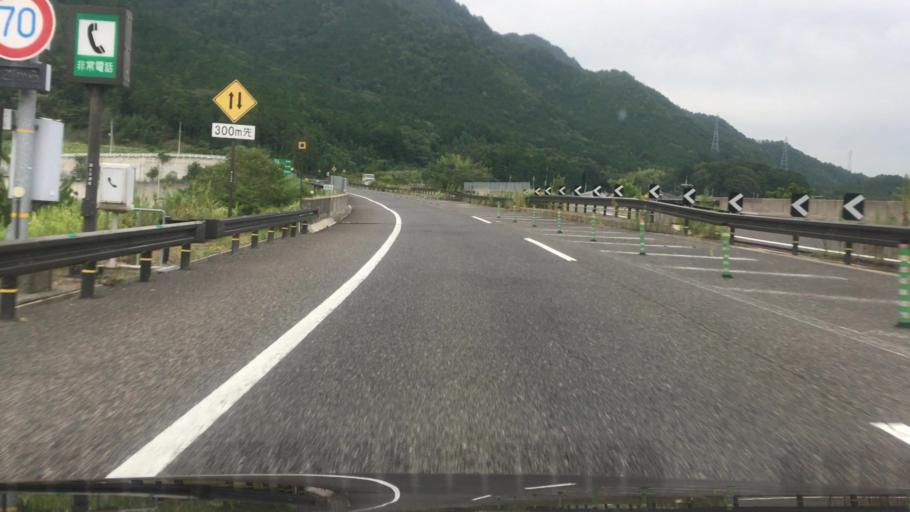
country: JP
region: Kyoto
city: Fukuchiyama
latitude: 35.1633
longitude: 135.0997
